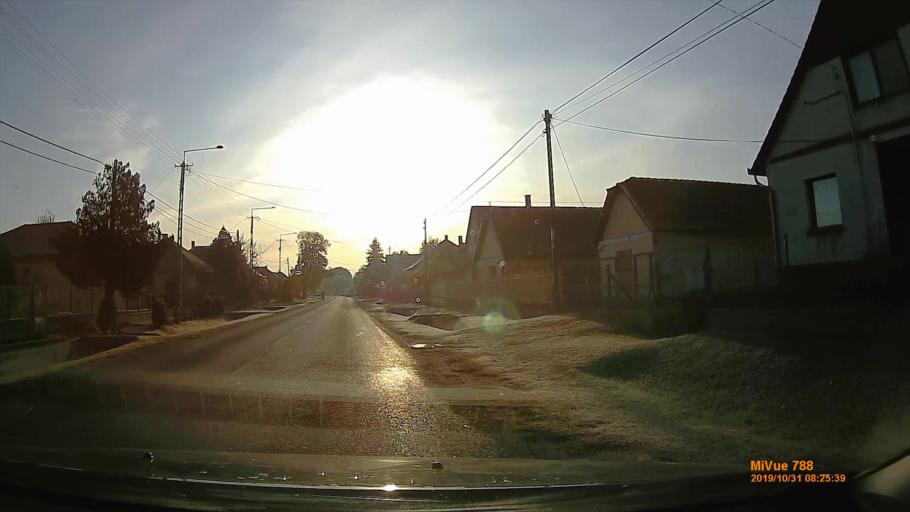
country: HU
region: Pest
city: Tapiobicske
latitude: 47.3653
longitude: 19.6709
